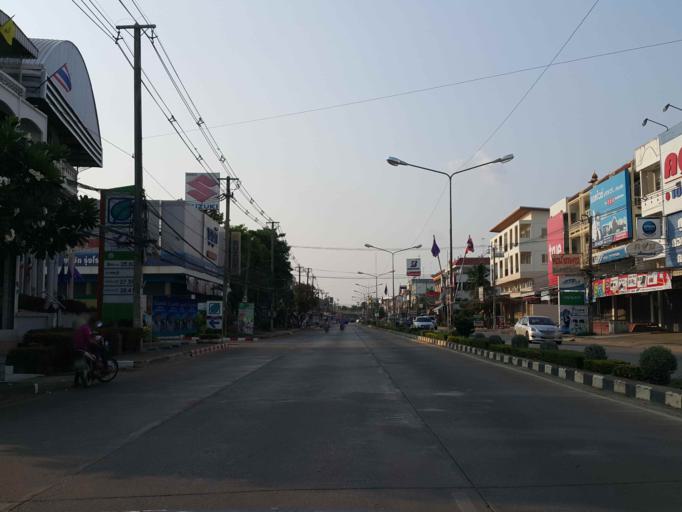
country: TH
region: Sukhothai
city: Sawankhalok
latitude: 17.3076
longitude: 99.8319
